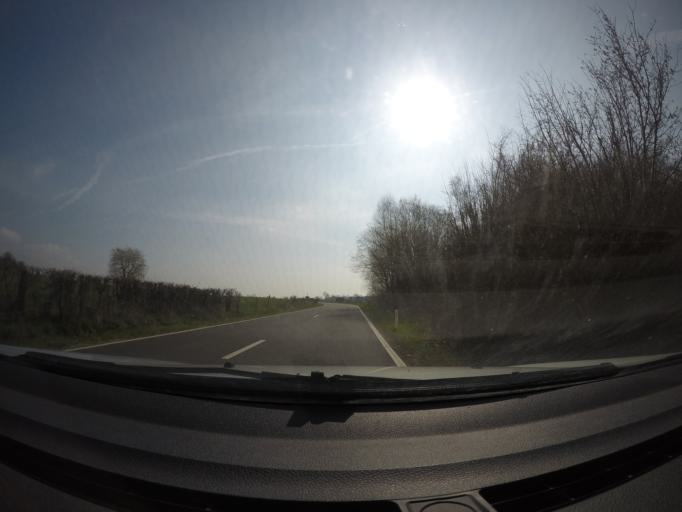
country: BE
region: Wallonia
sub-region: Province du Luxembourg
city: Tintigny
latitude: 49.7037
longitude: 5.4312
